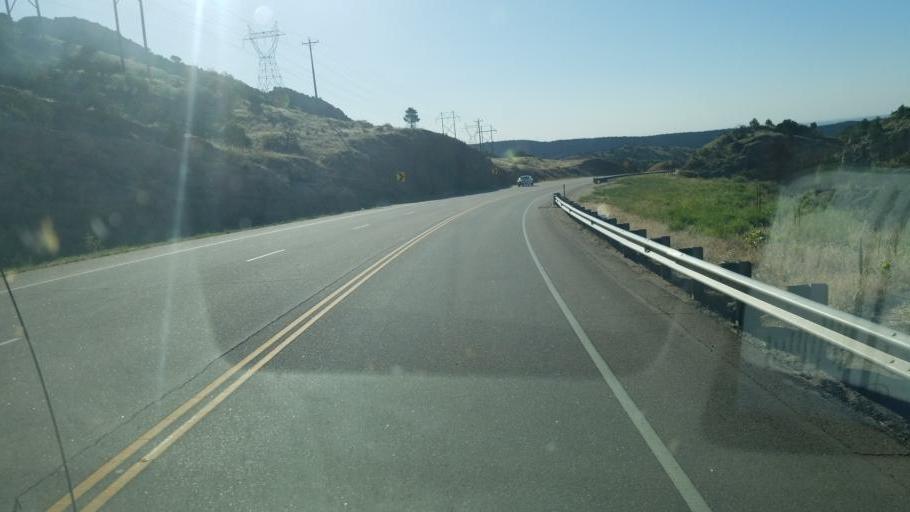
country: US
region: Colorado
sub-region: Fremont County
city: Canon City
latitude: 38.4957
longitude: -105.2896
